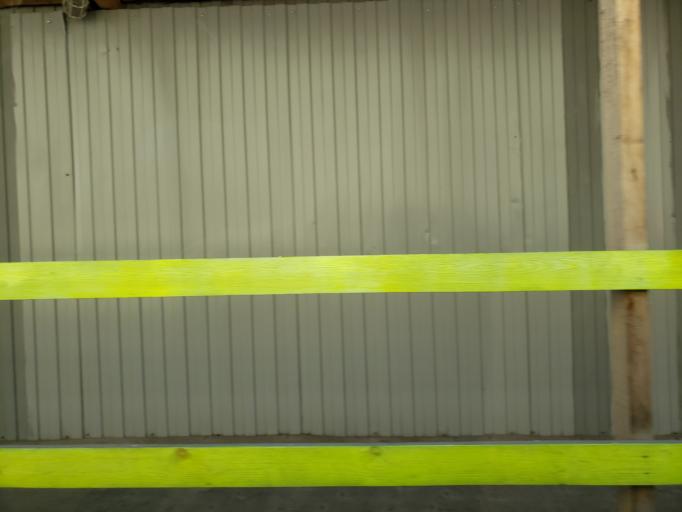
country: RU
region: St.-Petersburg
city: Saint Petersburg
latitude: 59.9436
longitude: 30.3269
